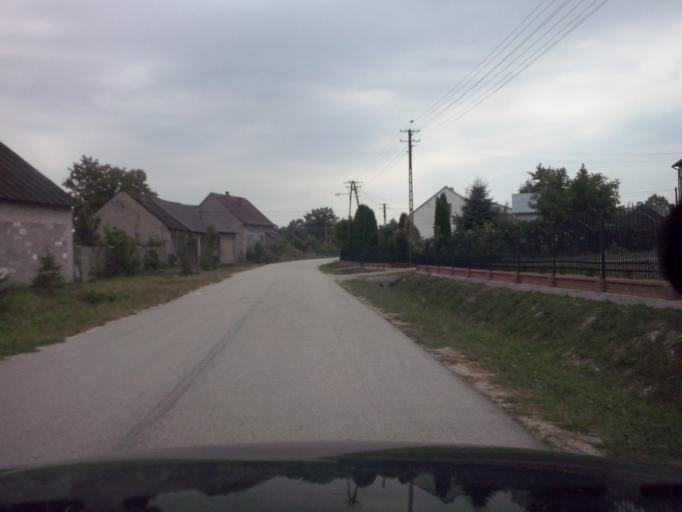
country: PL
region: Swietokrzyskie
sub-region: Powiat kielecki
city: Morawica
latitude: 50.6831
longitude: 20.6033
